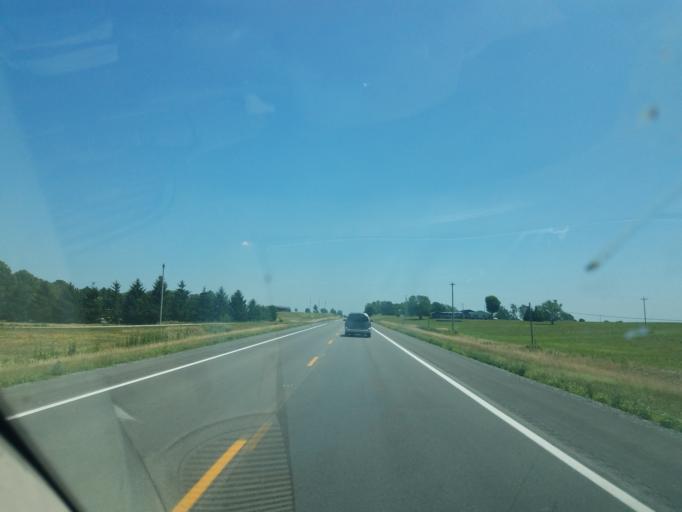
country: US
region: Ohio
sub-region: Hardin County
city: Ada
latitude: 40.7073
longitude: -83.7412
